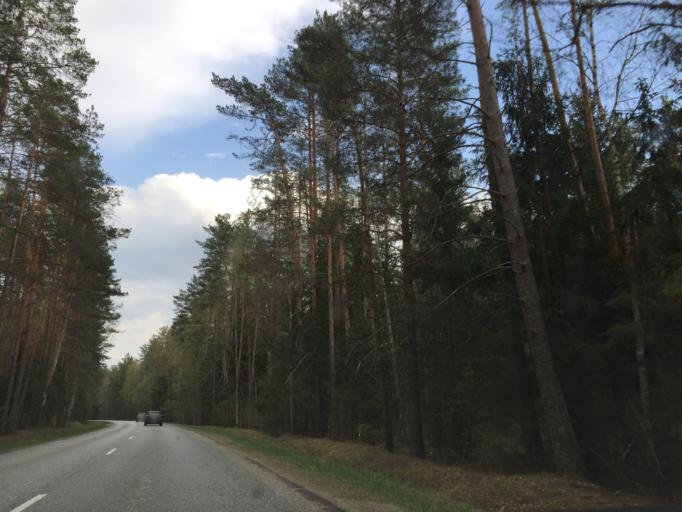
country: LV
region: Garkalne
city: Garkalne
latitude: 57.0096
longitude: 24.4682
